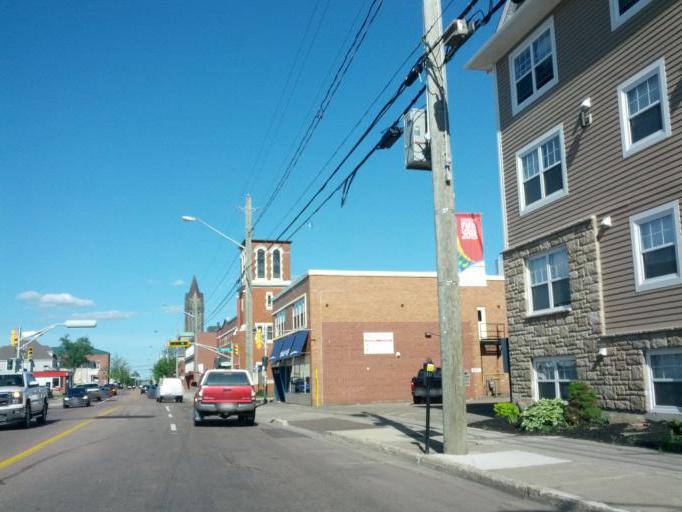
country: CA
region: New Brunswick
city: Moncton
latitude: 46.0903
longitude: -64.7865
